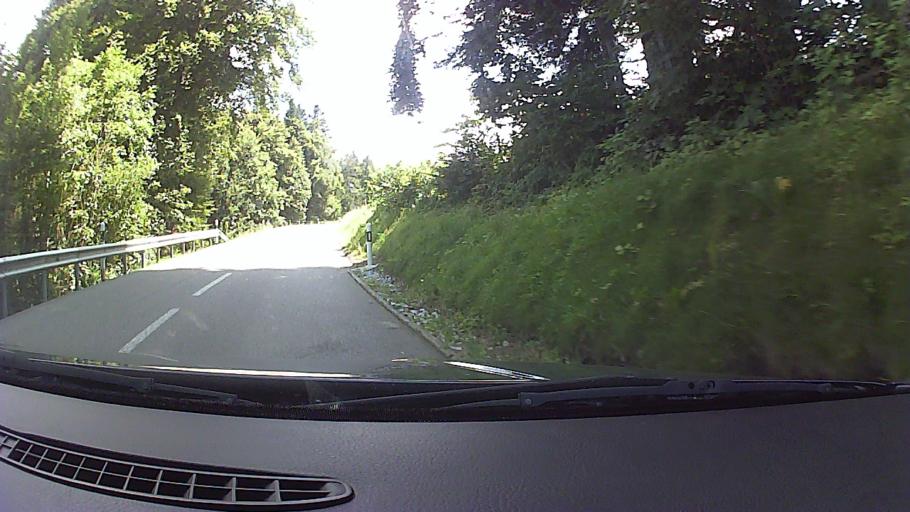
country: CH
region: Fribourg
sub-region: Veveyse District
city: Chatel-Saint-Denis
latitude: 46.5251
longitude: 6.9265
